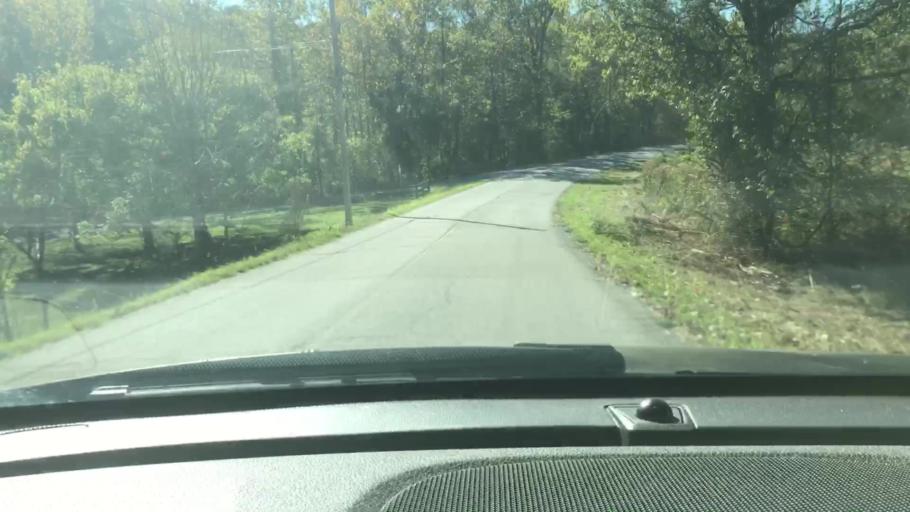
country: US
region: Tennessee
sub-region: Dickson County
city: Charlotte
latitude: 36.1798
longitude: -87.3045
